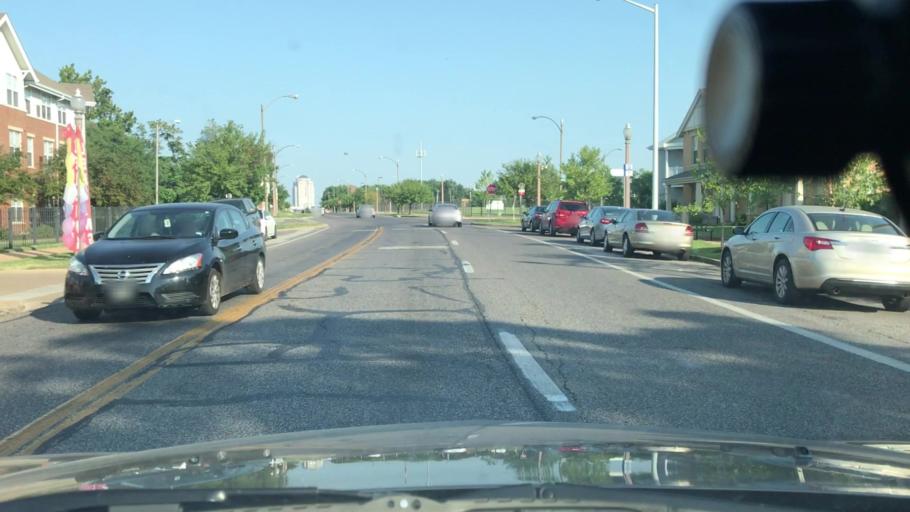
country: US
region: Missouri
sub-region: City of Saint Louis
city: St. Louis
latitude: 38.6442
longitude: -90.2246
